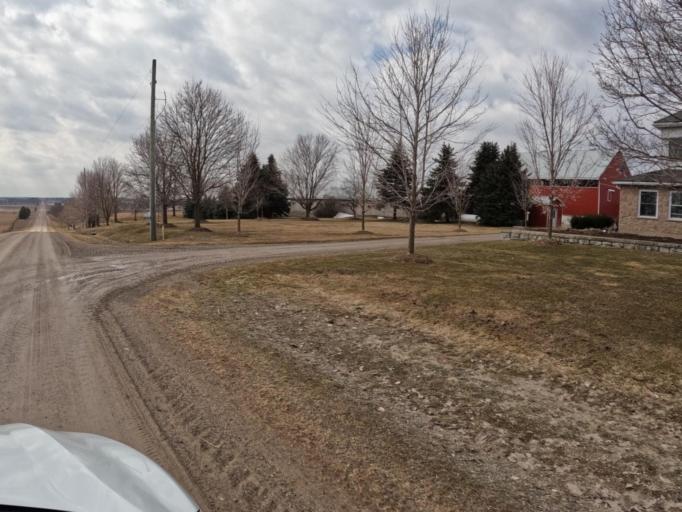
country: CA
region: Ontario
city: Orangeville
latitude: 43.9383
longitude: -80.2433
